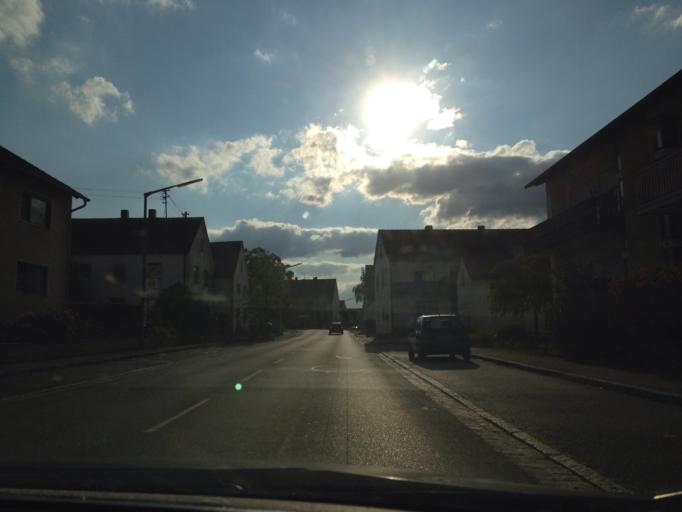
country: DE
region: Bavaria
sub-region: Upper Palatinate
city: Freystadt
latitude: 49.1715
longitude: 11.2880
